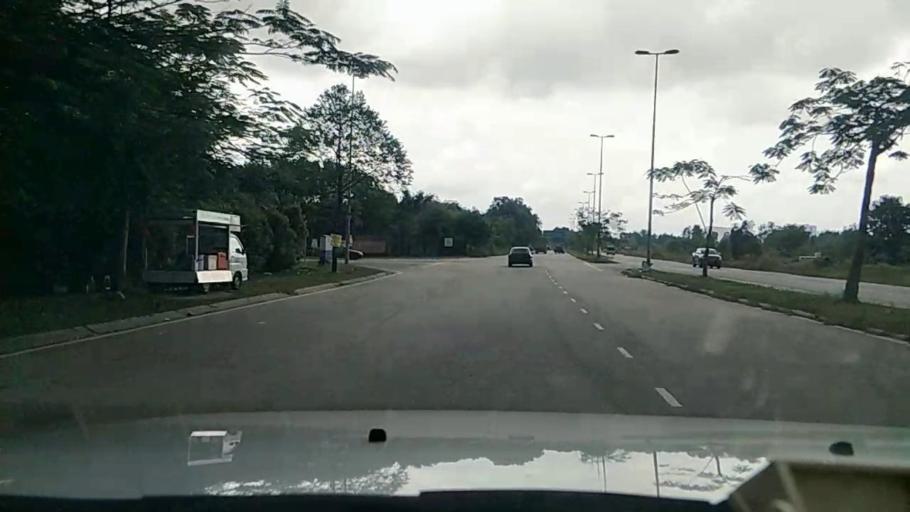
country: MY
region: Putrajaya
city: Putrajaya
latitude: 2.9349
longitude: 101.6195
